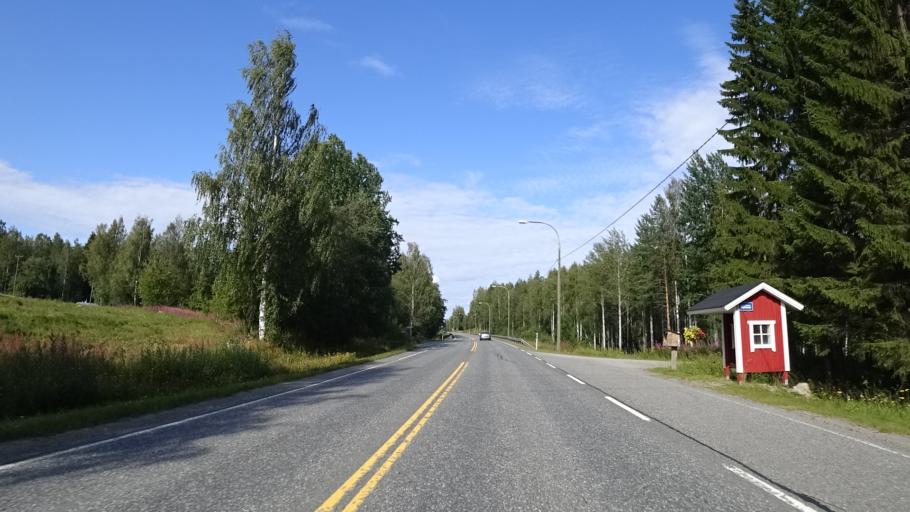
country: FI
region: North Karelia
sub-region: Joensuu
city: Eno
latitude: 62.7842
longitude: 30.0775
